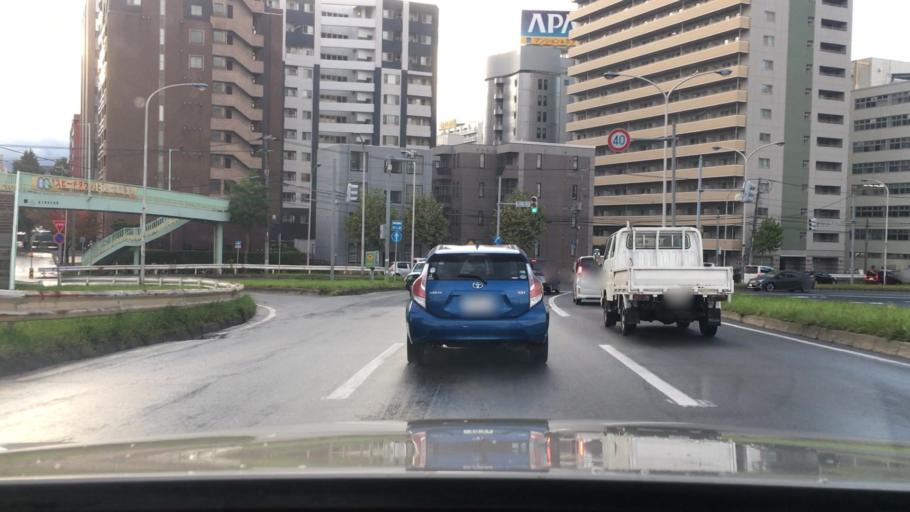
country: JP
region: Hokkaido
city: Sapporo
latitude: 43.0530
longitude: 141.3599
